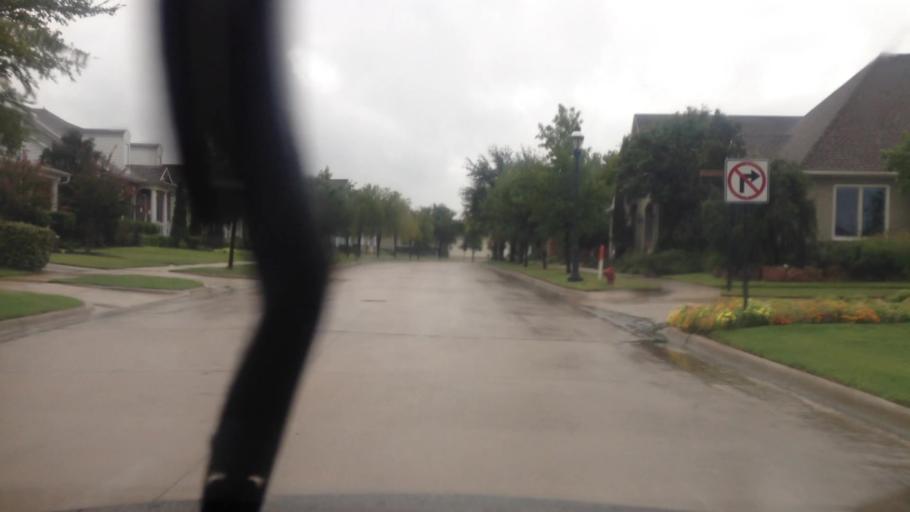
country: US
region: Texas
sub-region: Tarrant County
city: North Richland Hills
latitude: 32.8533
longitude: -97.2030
